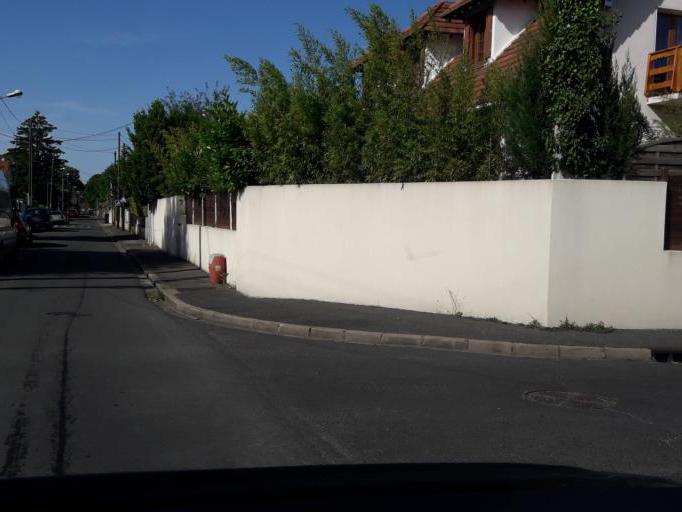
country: FR
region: Ile-de-France
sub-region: Departement de l'Essonne
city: Villemoisson-sur-Orge
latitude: 48.6532
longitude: 2.3338
